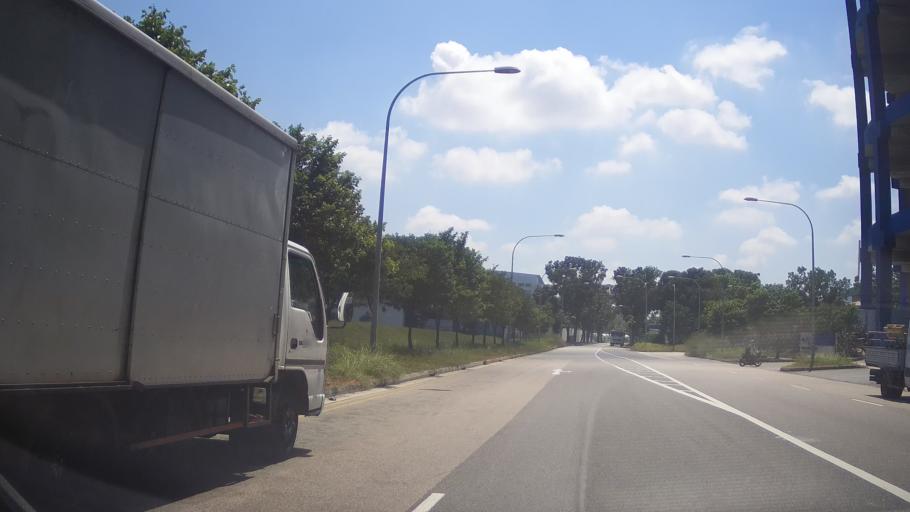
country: SG
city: Singapore
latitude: 1.3150
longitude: 103.7240
